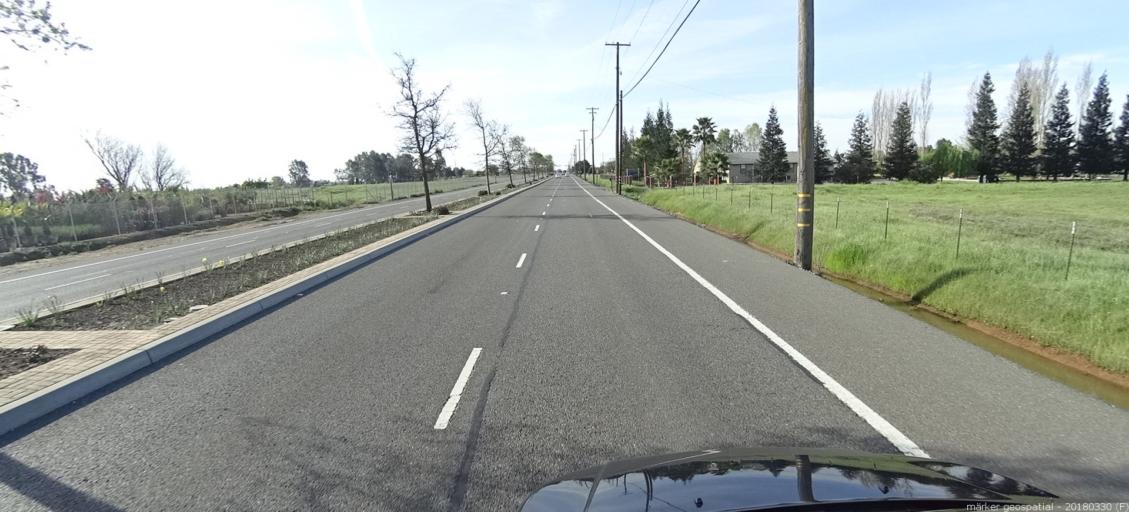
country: US
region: California
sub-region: Sacramento County
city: Vineyard
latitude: 38.5002
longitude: -121.3350
